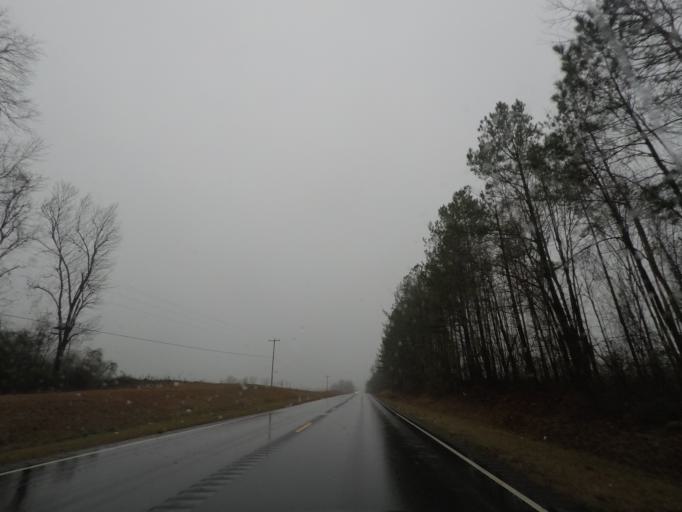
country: US
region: North Carolina
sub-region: Scotland County
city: Laurinburg
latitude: 34.8332
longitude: -79.4592
